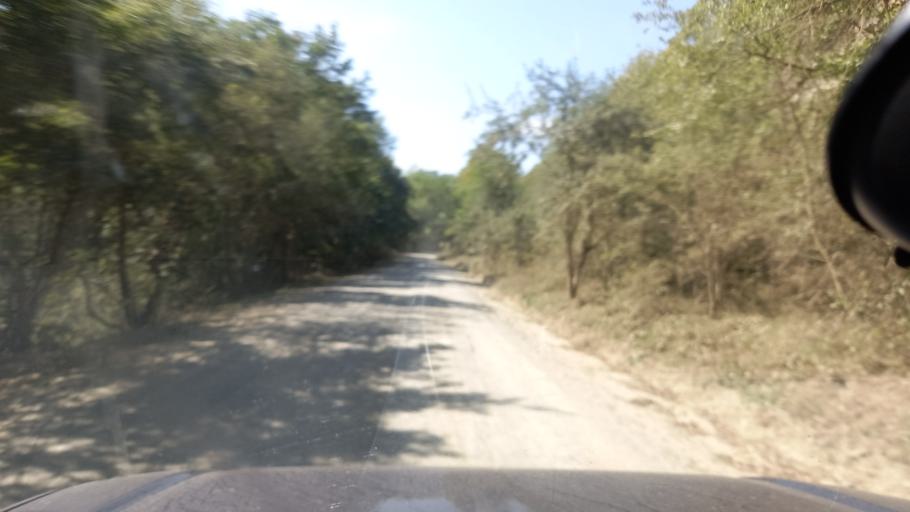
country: RU
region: Krasnodarskiy
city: Azovskaya
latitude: 44.6982
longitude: 38.6613
